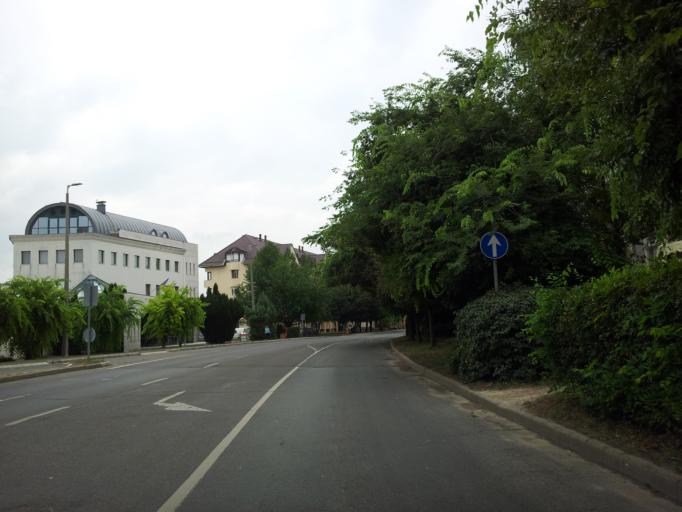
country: HU
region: Tolna
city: Tamasi
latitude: 46.6361
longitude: 18.2816
